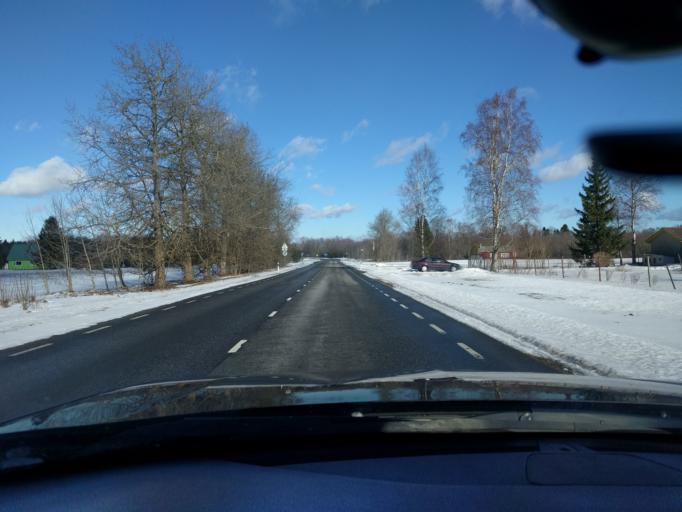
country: EE
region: Harju
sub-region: Raasiku vald
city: Raasiku
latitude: 59.3810
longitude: 25.1954
